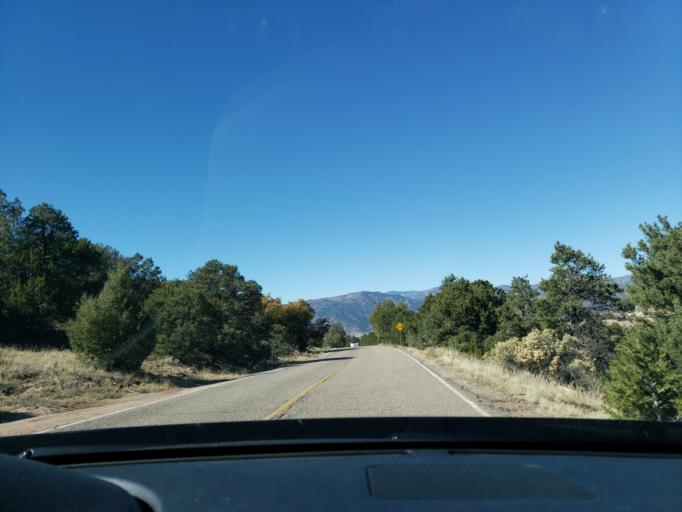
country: US
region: Colorado
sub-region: Fremont County
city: Canon City
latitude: 38.4635
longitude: -105.3148
